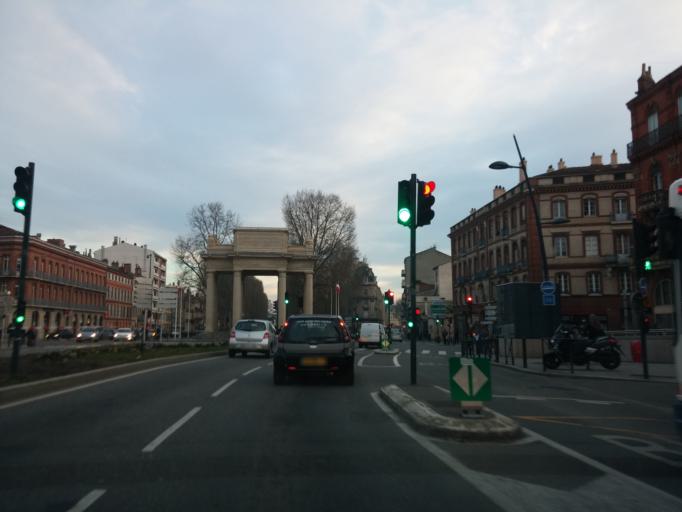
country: FR
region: Midi-Pyrenees
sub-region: Departement de la Haute-Garonne
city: Toulouse
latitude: 43.6008
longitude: 1.4519
